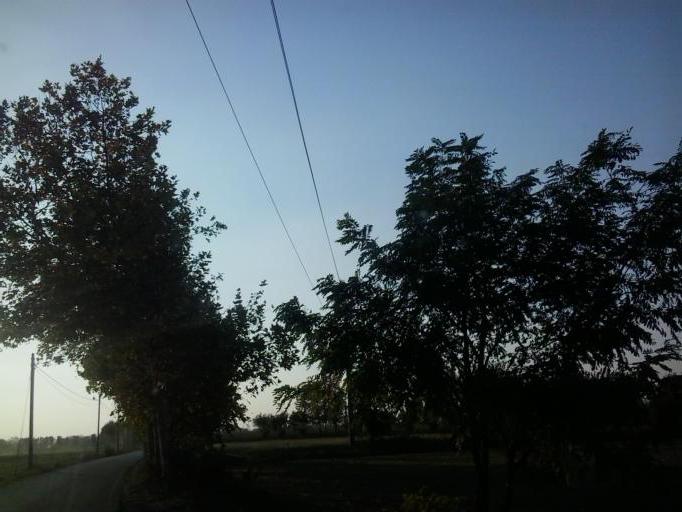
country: IT
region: Lombardy
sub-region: Provincia di Brescia
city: Capriano del Colle
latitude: 45.4685
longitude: 10.1435
